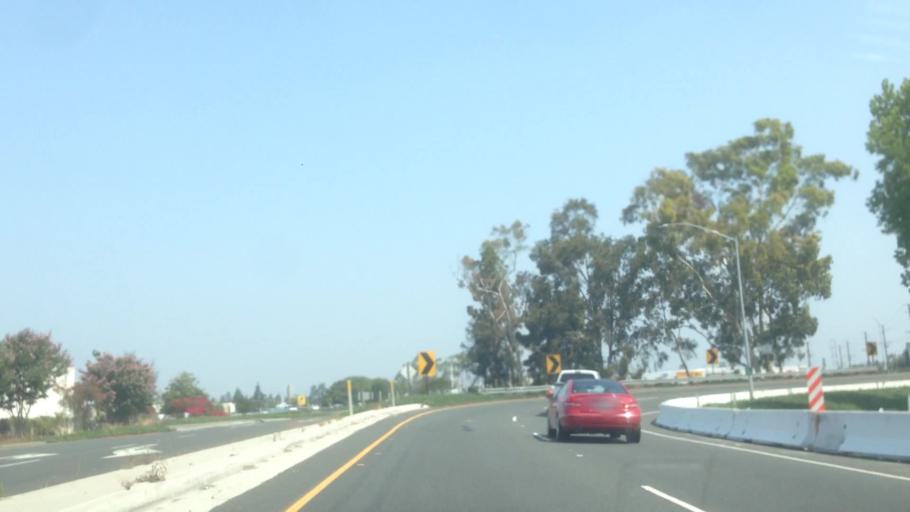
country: US
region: California
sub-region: Orange County
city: Fountain Valley
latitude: 33.6951
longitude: -117.9372
